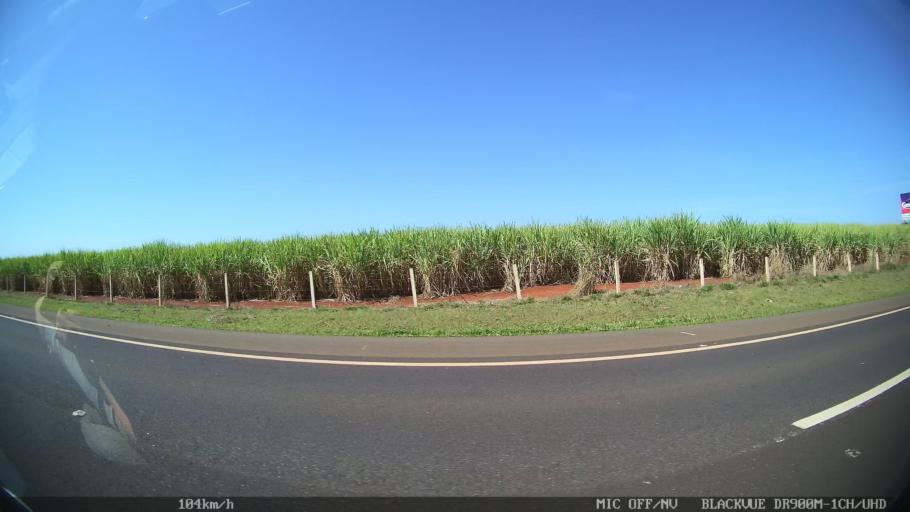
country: BR
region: Sao Paulo
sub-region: Batatais
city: Batatais
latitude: -20.7811
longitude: -47.5508
